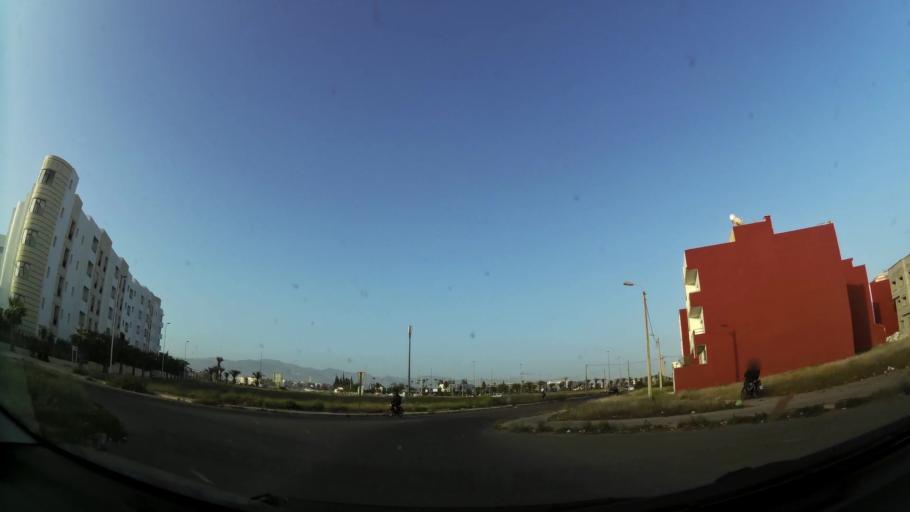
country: MA
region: Oued ed Dahab-Lagouira
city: Dakhla
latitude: 30.4017
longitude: -9.5734
